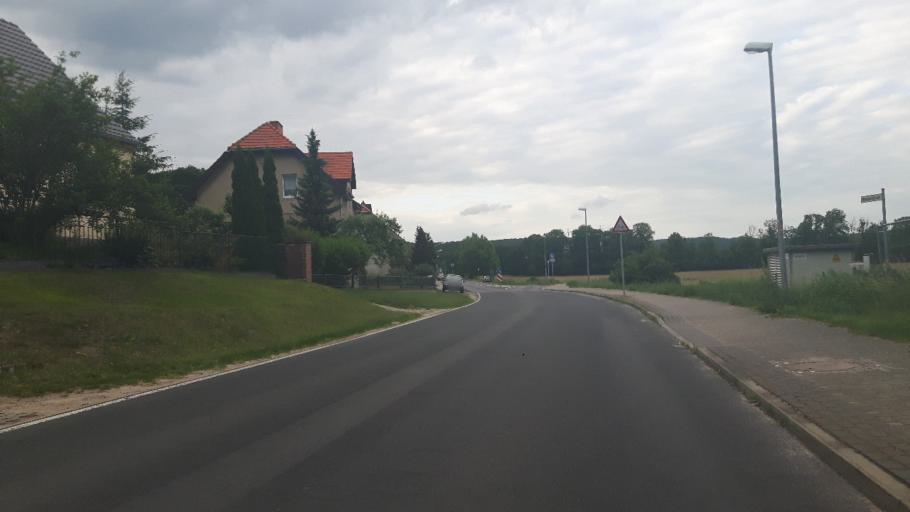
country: DE
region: Brandenburg
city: Niederfinow
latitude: 52.8379
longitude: 13.9370
